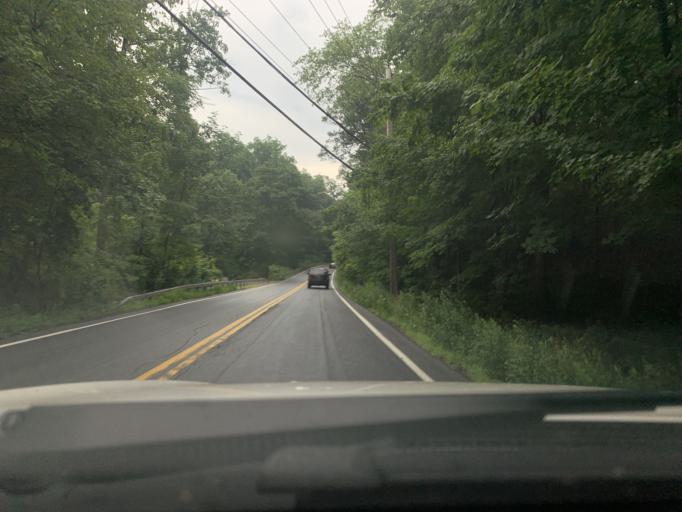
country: US
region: New York
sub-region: Westchester County
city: Ossining
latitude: 41.1894
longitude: -73.8408
